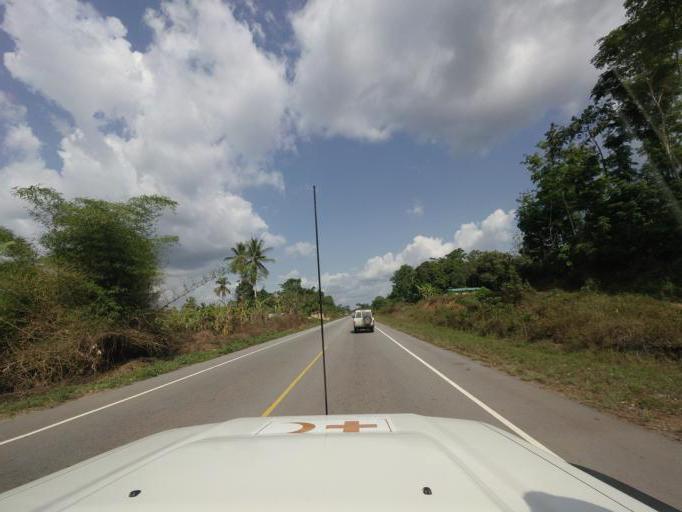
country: LR
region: Bong
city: Gbarnga
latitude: 6.8493
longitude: -9.8077
